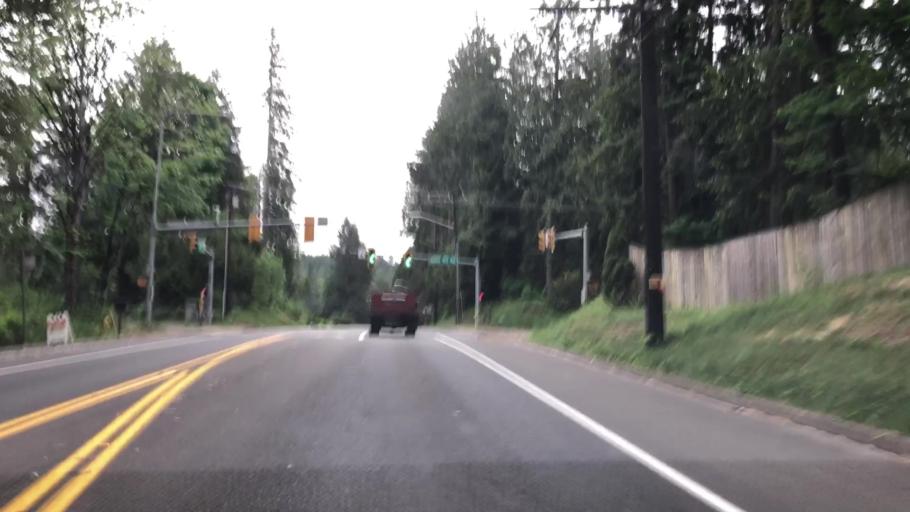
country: US
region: Washington
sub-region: King County
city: Cottage Lake
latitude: 47.7549
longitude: -122.0627
